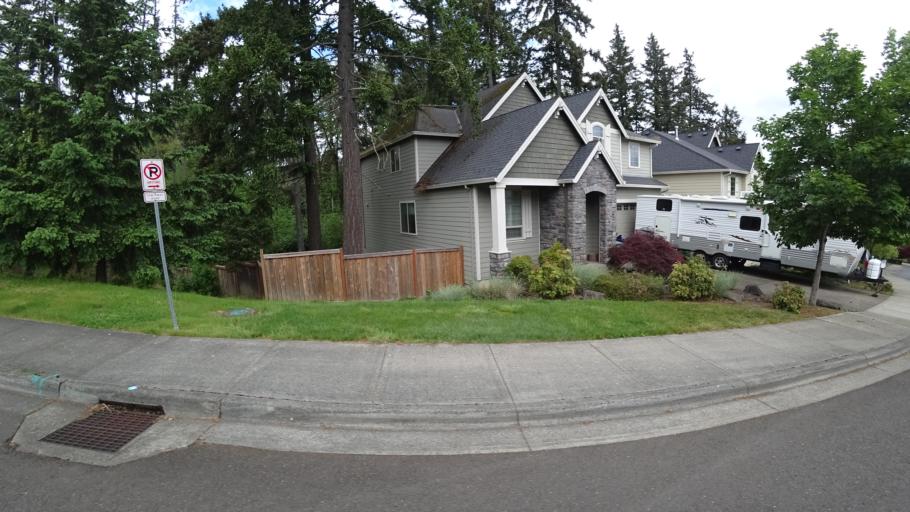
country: US
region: Oregon
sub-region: Washington County
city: Aloha
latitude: 45.4649
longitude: -122.8585
